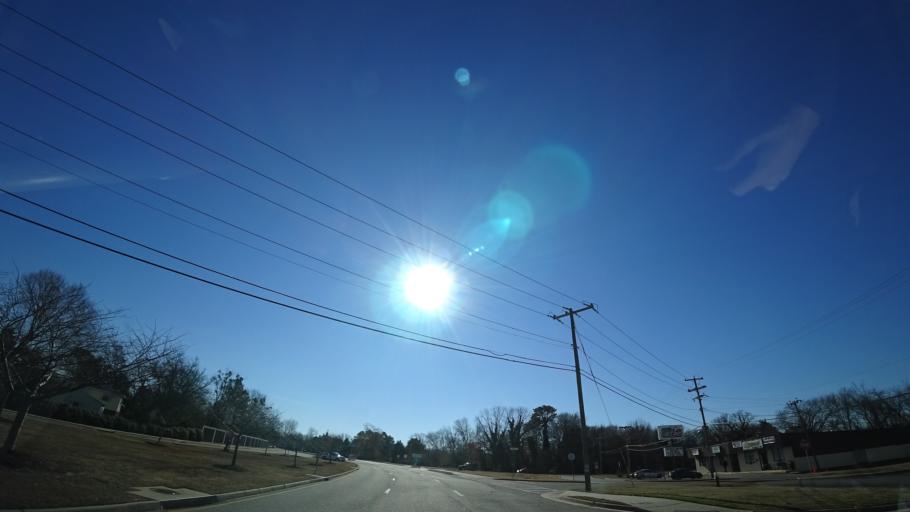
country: US
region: Virginia
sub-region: City of Hampton
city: Hampton
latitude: 37.0419
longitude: -76.3766
